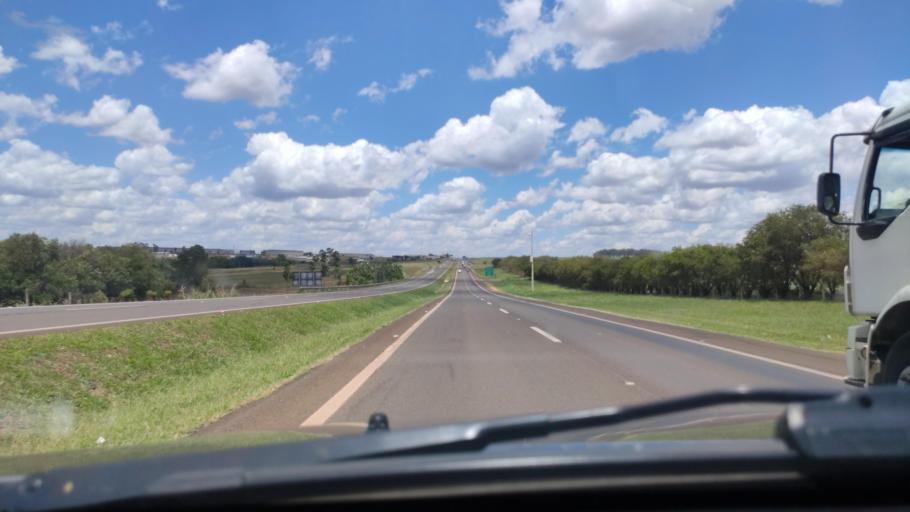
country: BR
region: Sao Paulo
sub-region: Pederneiras
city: Pederneiras
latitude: -22.3299
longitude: -48.7521
